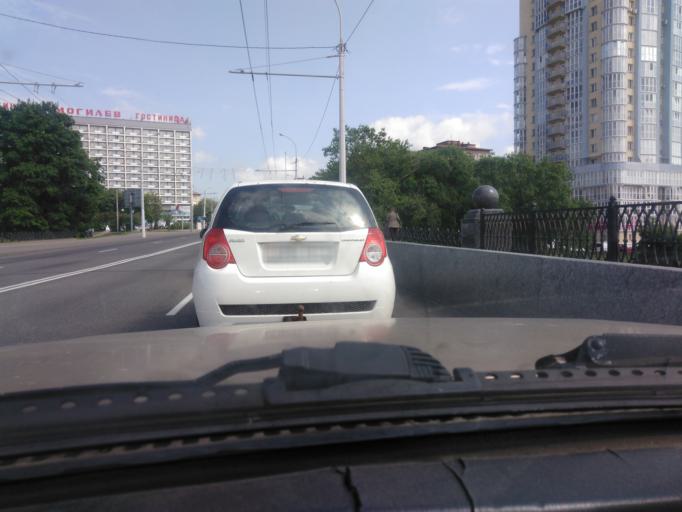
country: BY
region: Mogilev
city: Mahilyow
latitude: 53.9103
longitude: 30.3295
